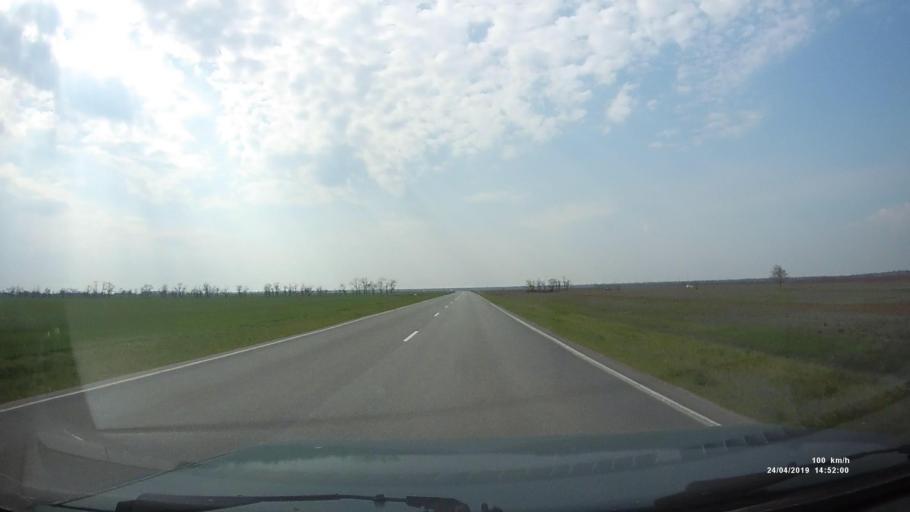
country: RU
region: Rostov
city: Remontnoye
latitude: 46.5288
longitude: 43.6898
